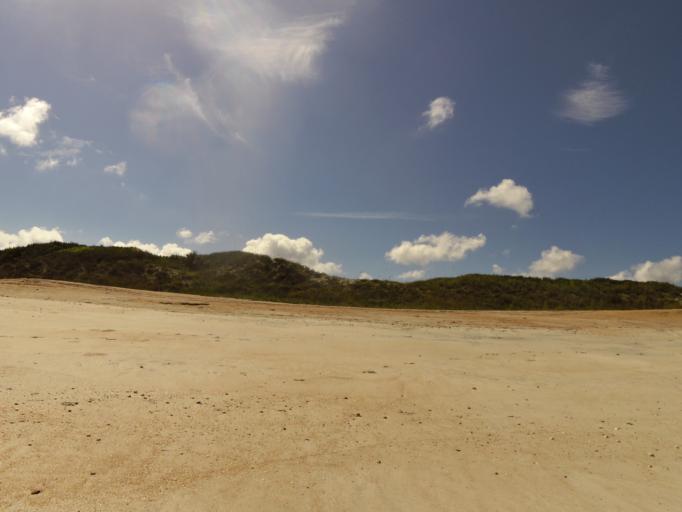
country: US
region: Florida
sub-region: Saint Johns County
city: Palm Valley
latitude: 30.0774
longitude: -81.3350
